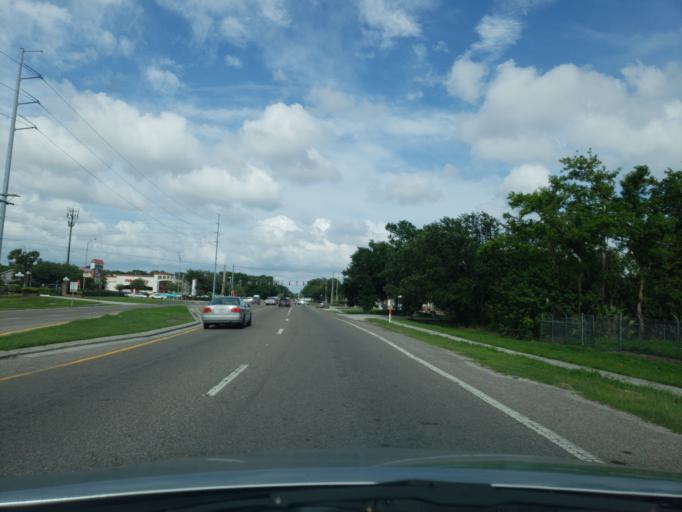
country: US
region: Florida
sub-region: Hillsborough County
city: Egypt Lake-Leto
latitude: 28.0071
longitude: -82.5067
